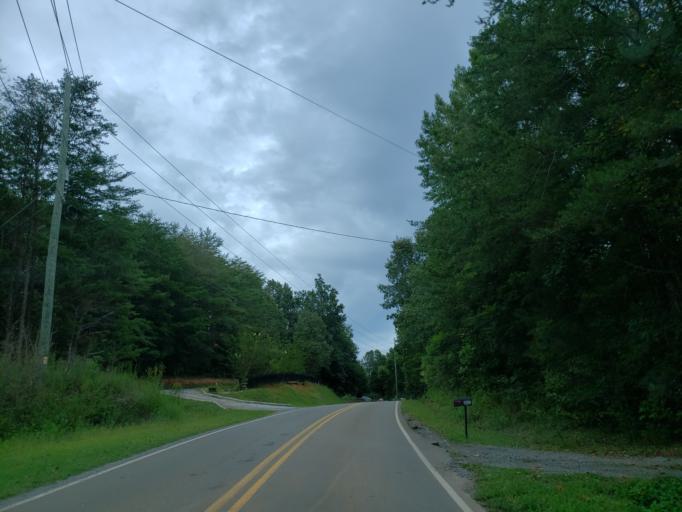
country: US
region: Georgia
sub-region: Pickens County
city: Jasper
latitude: 34.4215
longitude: -84.5533
